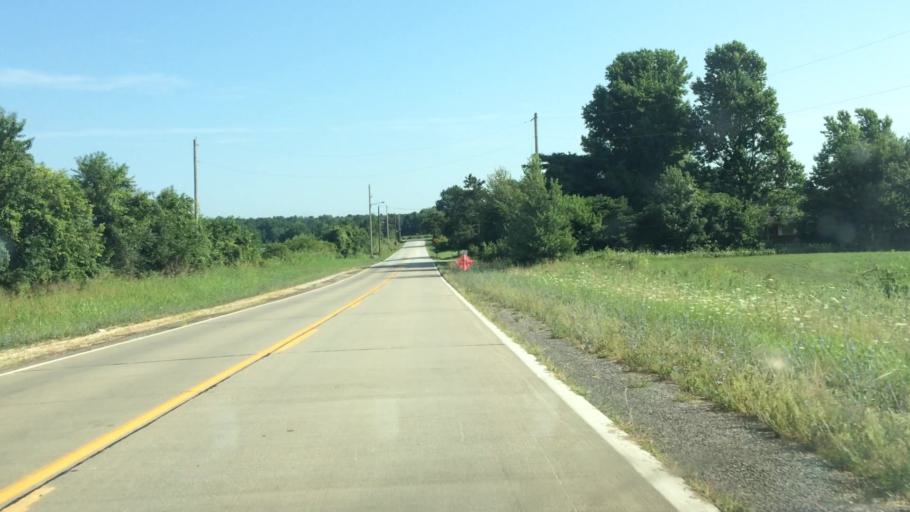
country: US
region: Missouri
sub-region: Greene County
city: Strafford
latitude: 37.2528
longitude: -93.1832
